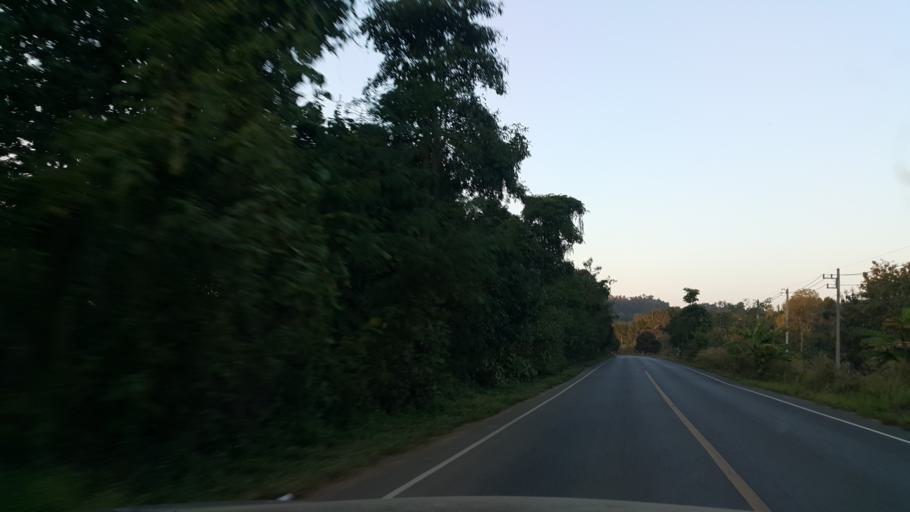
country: TH
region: Phrae
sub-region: Amphoe Wang Chin
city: Wang Chin
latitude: 17.8425
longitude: 99.6417
